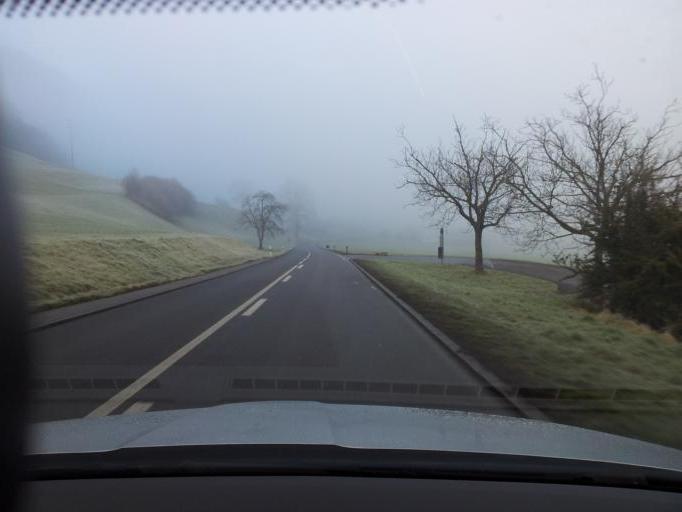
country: CH
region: Lucerne
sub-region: Lucerne-Stadt District
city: Littau
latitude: 47.0408
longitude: 8.2363
